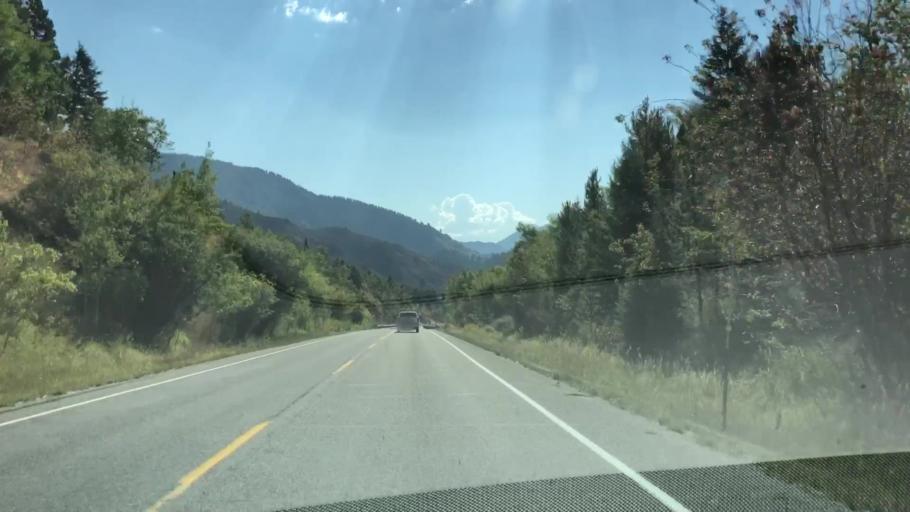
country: US
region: Wyoming
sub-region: Teton County
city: Hoback
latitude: 43.2262
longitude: -111.0824
